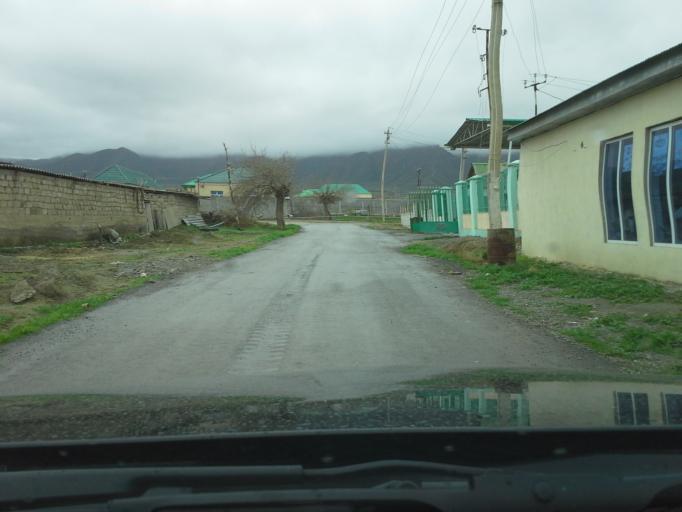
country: TM
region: Ahal
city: Abadan
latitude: 37.9693
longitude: 58.2072
